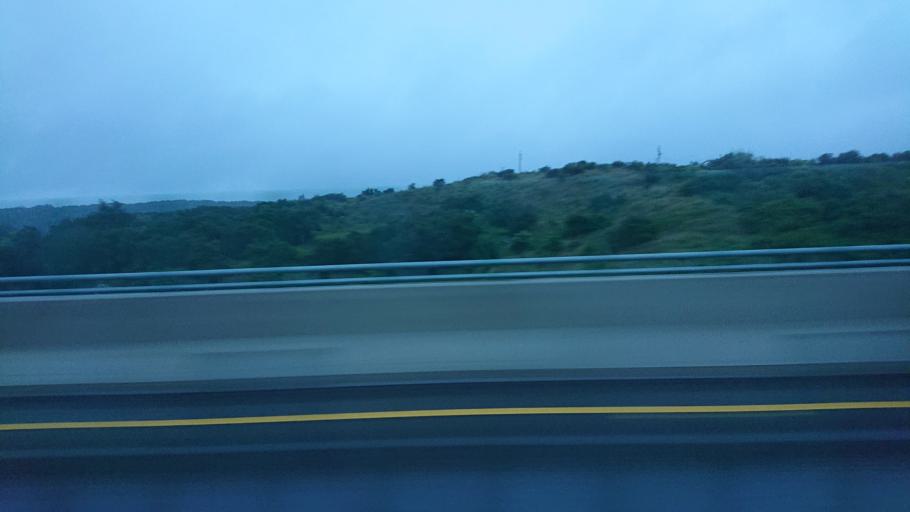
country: TW
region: Taiwan
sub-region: Miaoli
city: Miaoli
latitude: 24.5701
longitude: 120.7157
